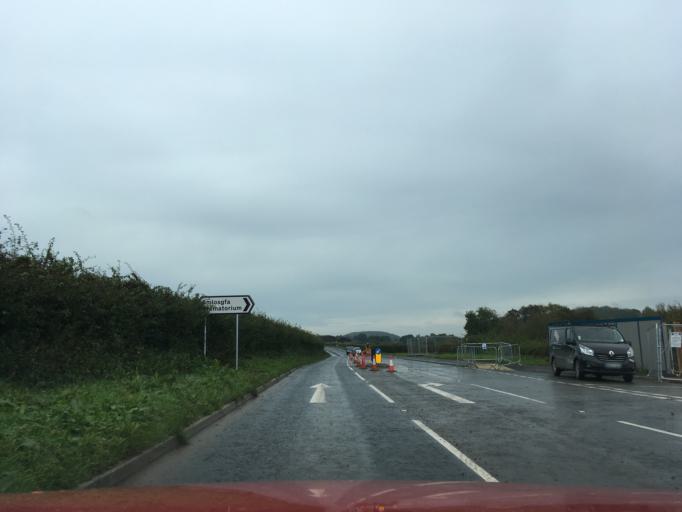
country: GB
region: Wales
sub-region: Newport
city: Bishton
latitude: 51.6038
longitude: -2.8851
